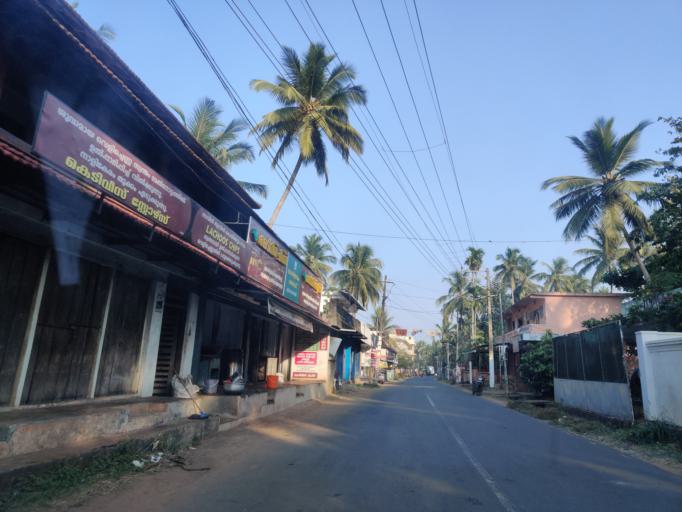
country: IN
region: Kerala
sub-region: Malappuram
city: Ponnani
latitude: 10.7338
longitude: 76.0137
